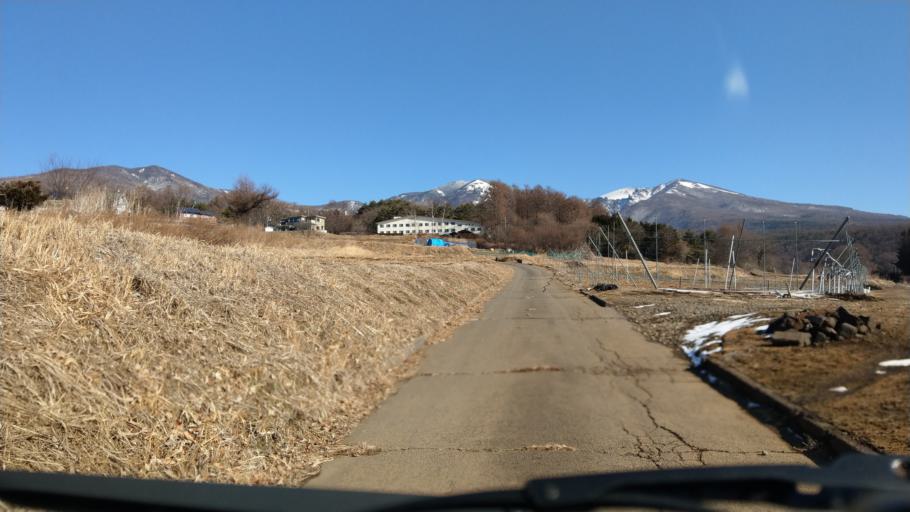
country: JP
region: Nagano
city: Komoro
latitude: 36.3583
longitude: 138.4459
